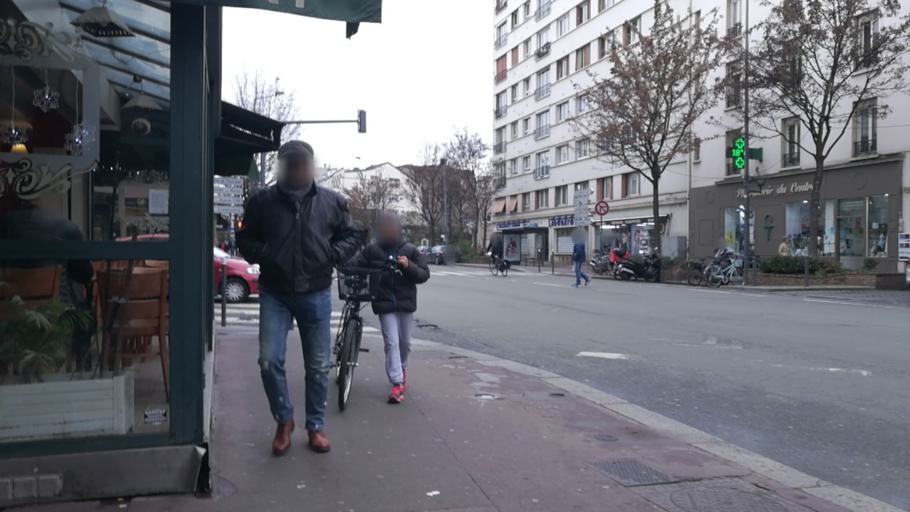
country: FR
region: Ile-de-France
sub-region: Paris
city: Saint-Ouen
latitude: 48.9085
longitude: 2.3327
